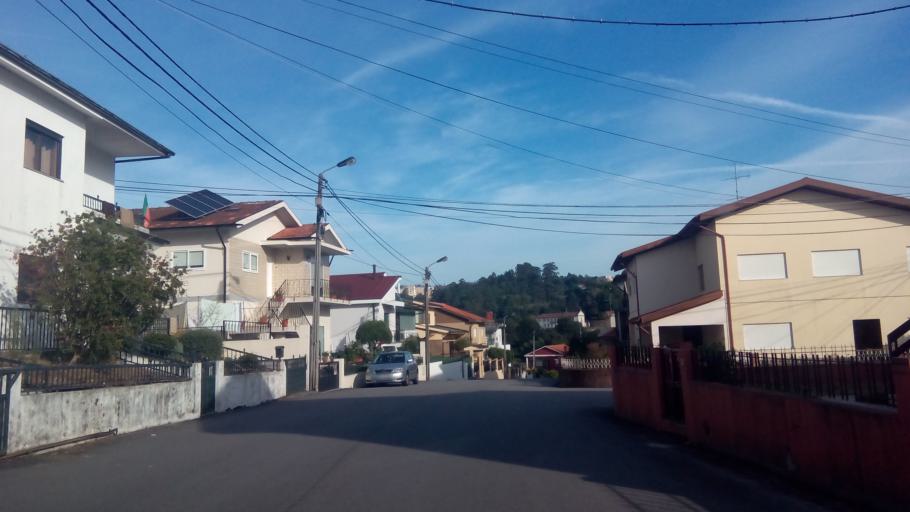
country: PT
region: Porto
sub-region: Paredes
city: Paredes
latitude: 41.2012
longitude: -8.3248
